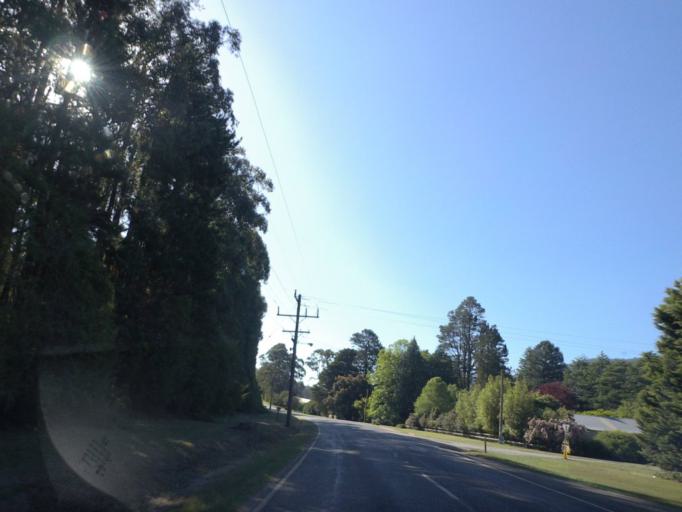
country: AU
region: Victoria
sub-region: Yarra Ranges
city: Yarra Junction
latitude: -37.8457
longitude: 145.6860
